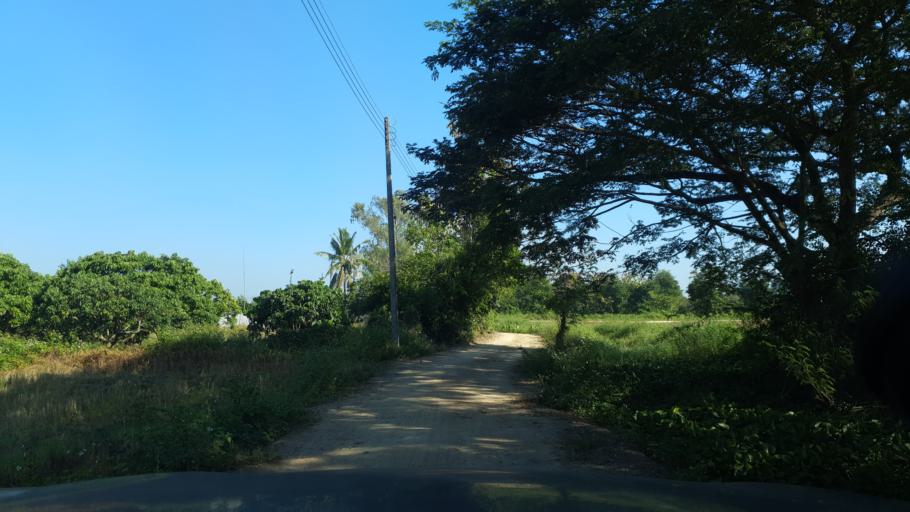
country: TH
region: Chiang Mai
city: Saraphi
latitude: 18.7185
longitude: 99.0750
